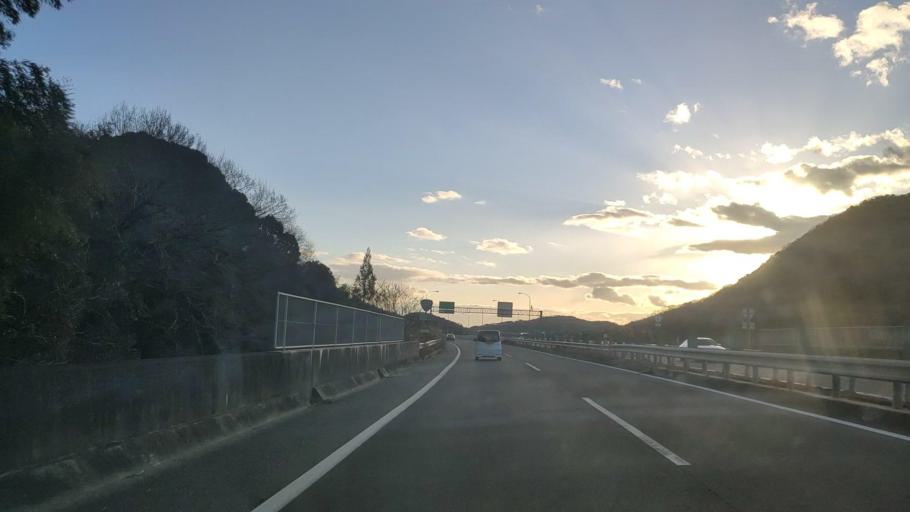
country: JP
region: Hyogo
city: Tatsunocho-tominaga
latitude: 34.8547
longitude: 134.6067
